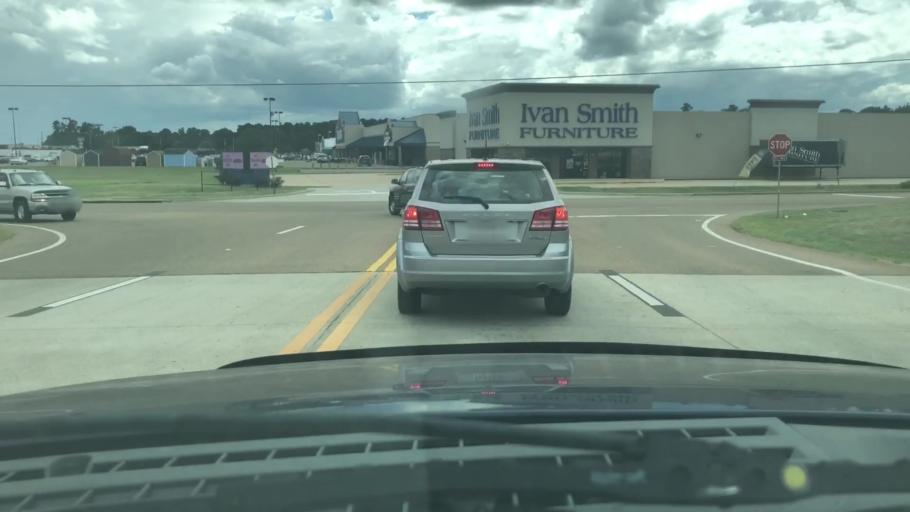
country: US
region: Texas
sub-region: Bowie County
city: Wake Village
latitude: 33.4500
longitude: -94.1001
